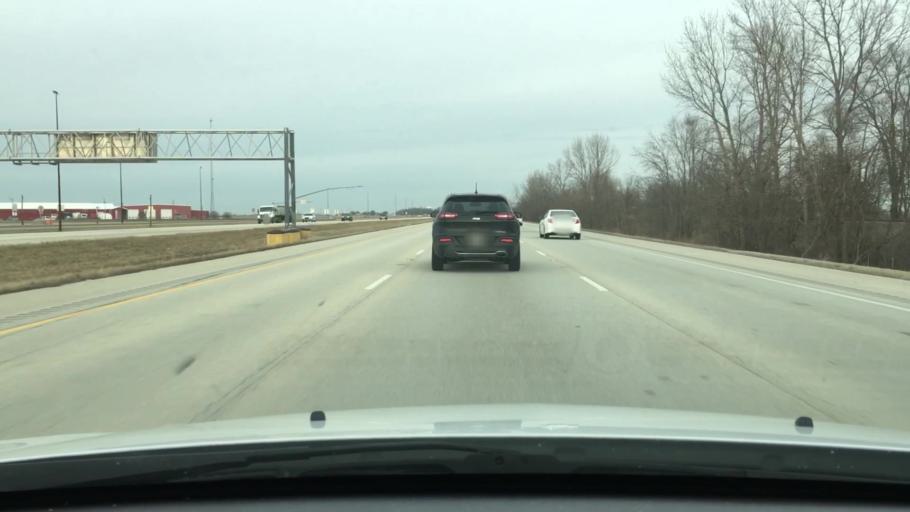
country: US
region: Illinois
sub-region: Sangamon County
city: Williamsville
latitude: 39.9287
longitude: -89.5723
